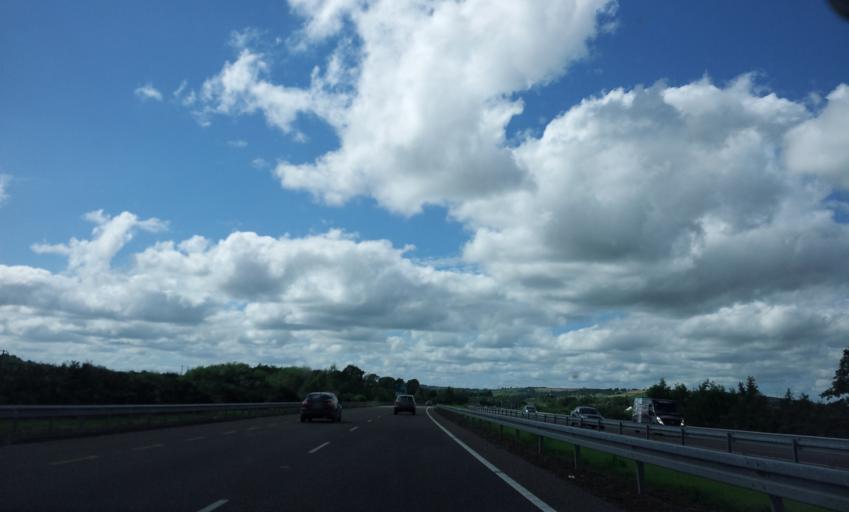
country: IE
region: Munster
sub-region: County Cork
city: Tower
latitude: 51.8730
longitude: -8.5969
